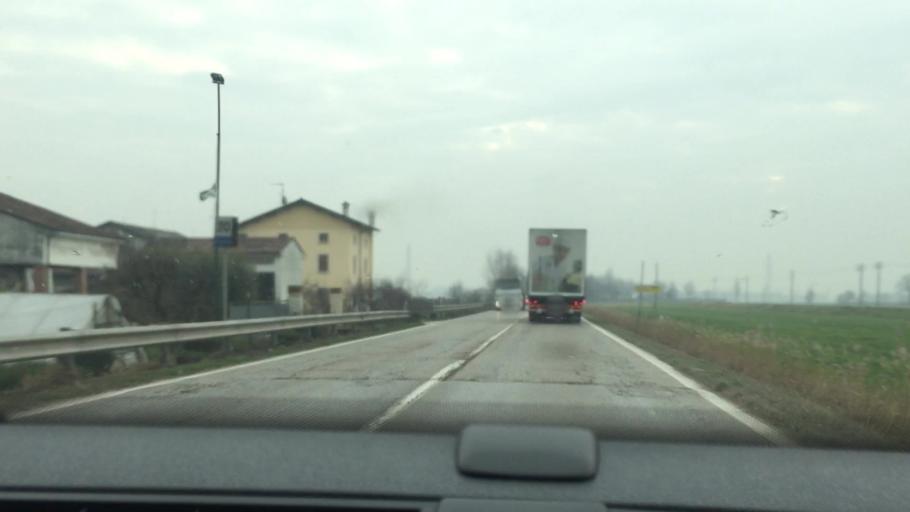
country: IT
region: Lombardy
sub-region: Provincia di Mantova
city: Cerlongo
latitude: 45.2974
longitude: 10.6196
